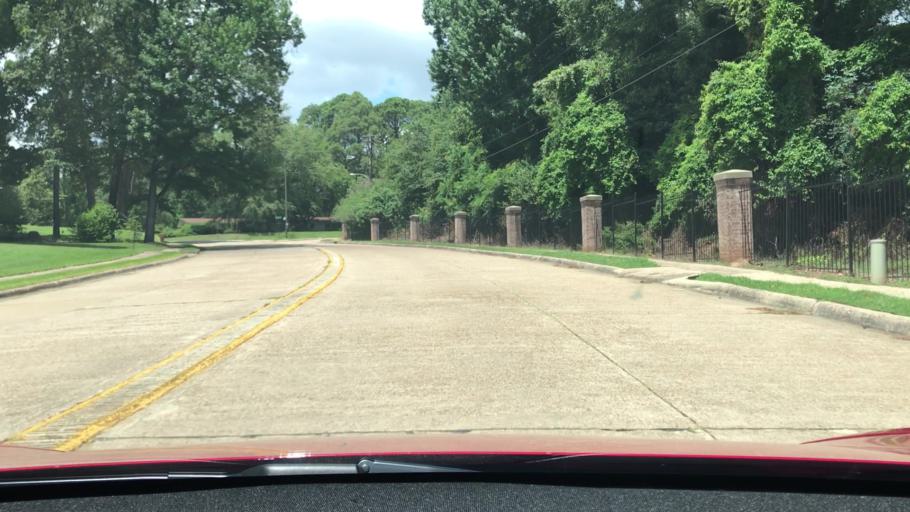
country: US
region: Louisiana
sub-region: Bossier Parish
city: Bossier City
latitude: 32.4356
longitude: -93.7312
